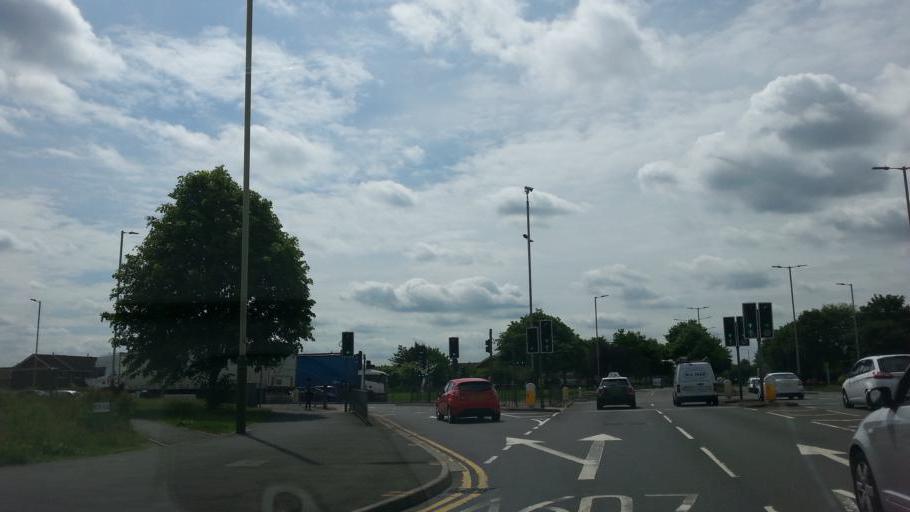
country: GB
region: England
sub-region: City of Leicester
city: Leicester
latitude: 52.6680
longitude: -1.1073
